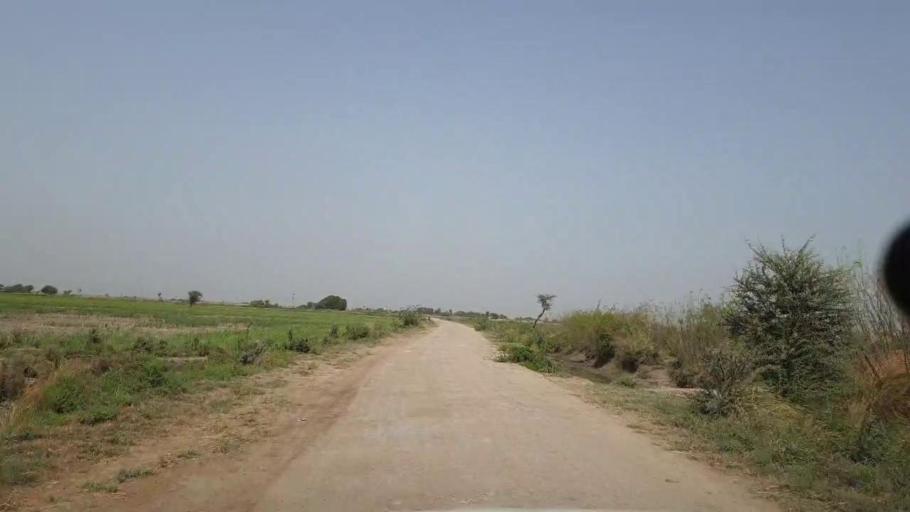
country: PK
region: Sindh
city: Matli
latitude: 25.0704
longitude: 68.6898
